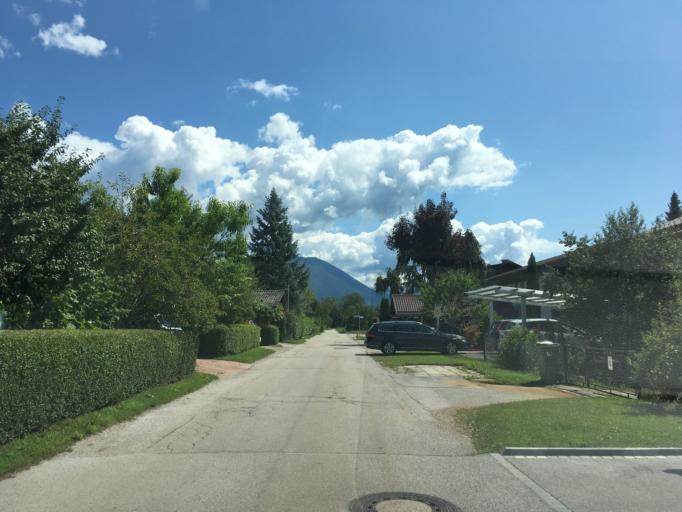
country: SI
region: Bled
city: Bled
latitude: 46.3705
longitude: 14.1231
